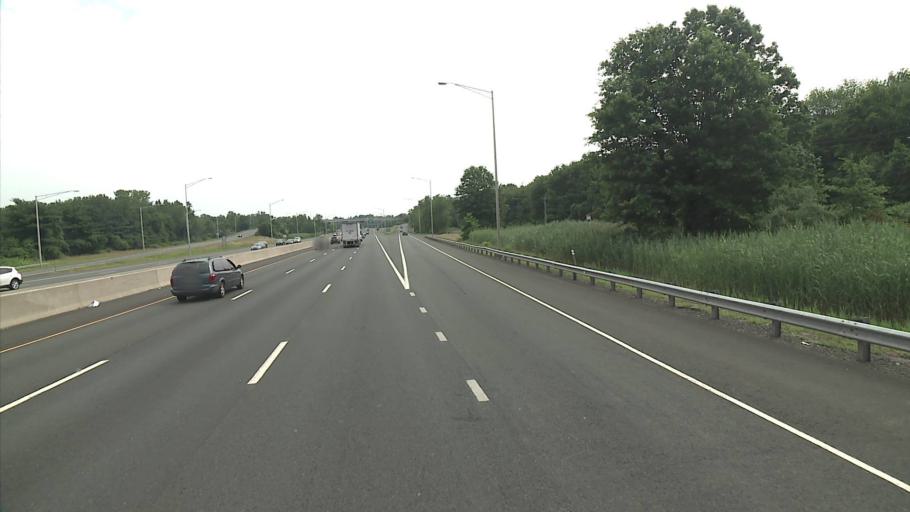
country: US
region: Connecticut
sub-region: New Haven County
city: Cheshire Village
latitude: 41.5574
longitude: -72.9233
